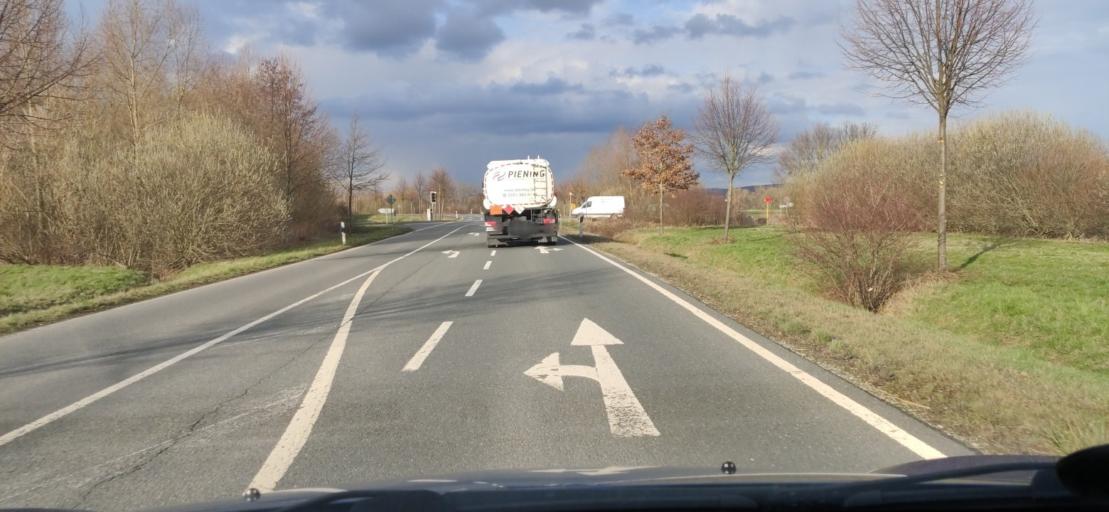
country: DE
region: Lower Saxony
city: Rosdorf
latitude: 51.4992
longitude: 9.9122
